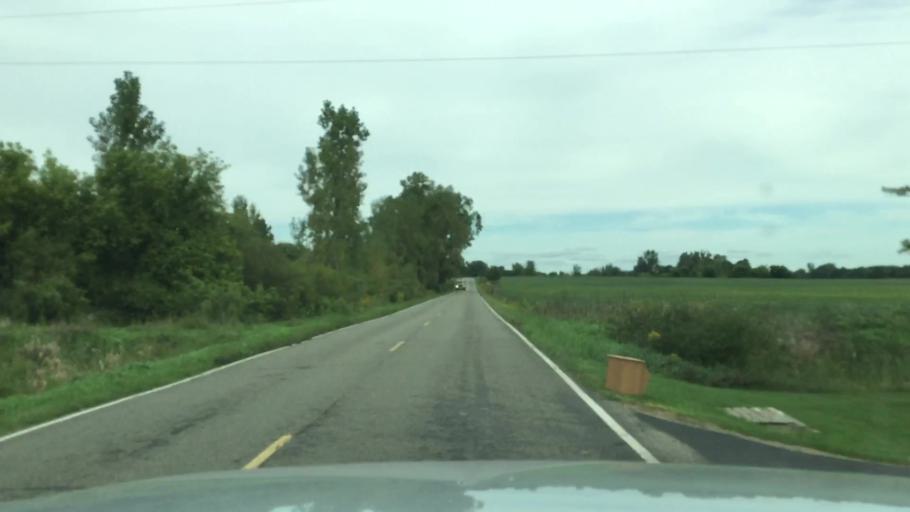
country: US
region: Michigan
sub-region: Shiawassee County
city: Durand
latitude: 42.9330
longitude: -83.9588
